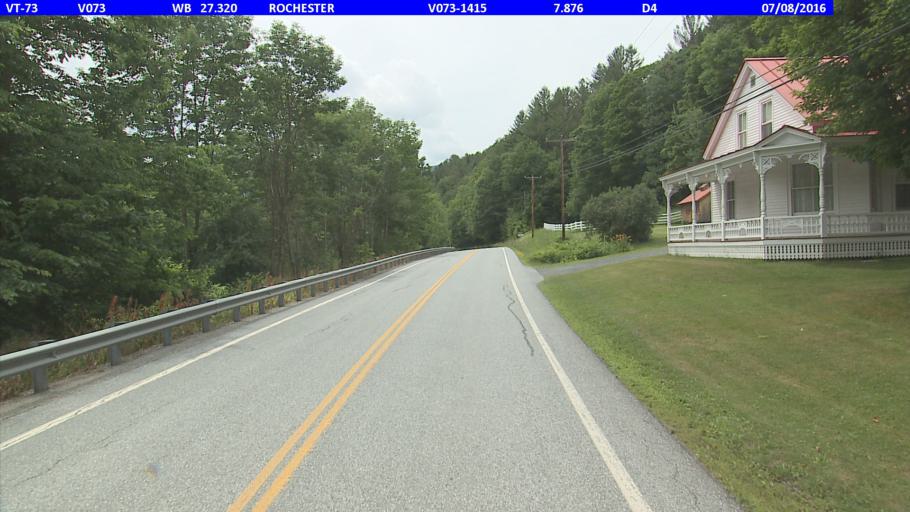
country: US
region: Vermont
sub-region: Orange County
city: Randolph
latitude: 43.8552
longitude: -72.8216
